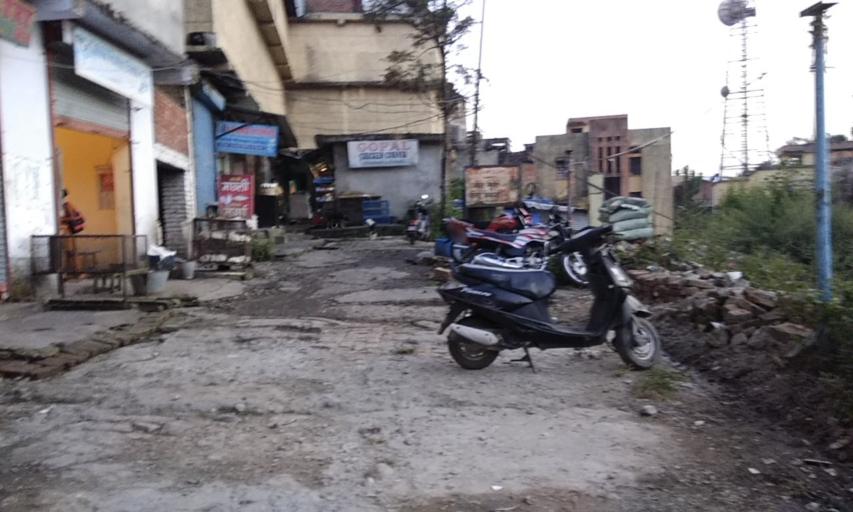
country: IN
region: Himachal Pradesh
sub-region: Kangra
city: Palampur
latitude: 32.1116
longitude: 76.5359
